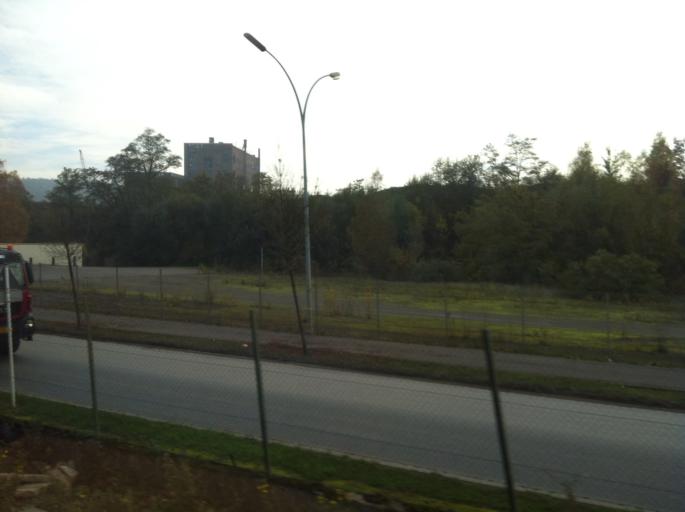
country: LU
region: Luxembourg
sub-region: Canton d'Esch-sur-Alzette
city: Esch-sur-Alzette
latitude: 49.4943
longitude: 5.9676
